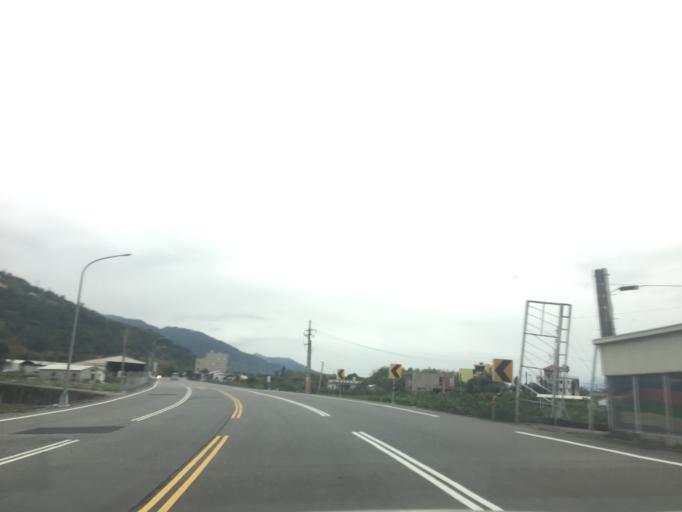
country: TW
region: Taiwan
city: Taitung City
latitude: 22.7269
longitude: 121.0563
